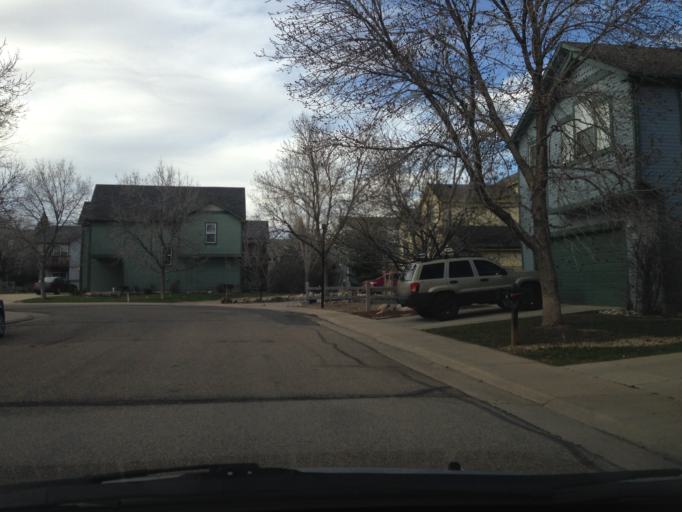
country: US
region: Colorado
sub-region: Boulder County
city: Louisville
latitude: 39.9984
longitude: -105.1157
